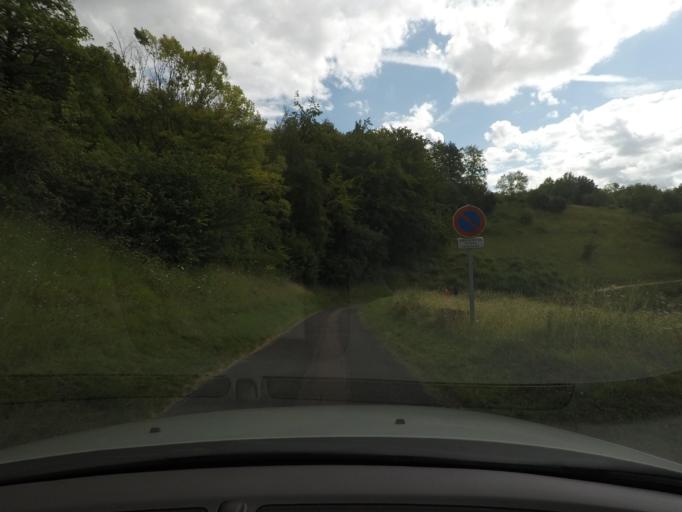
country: FR
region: Haute-Normandie
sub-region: Departement de l'Eure
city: Les Andelys
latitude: 49.2379
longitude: 1.4066
